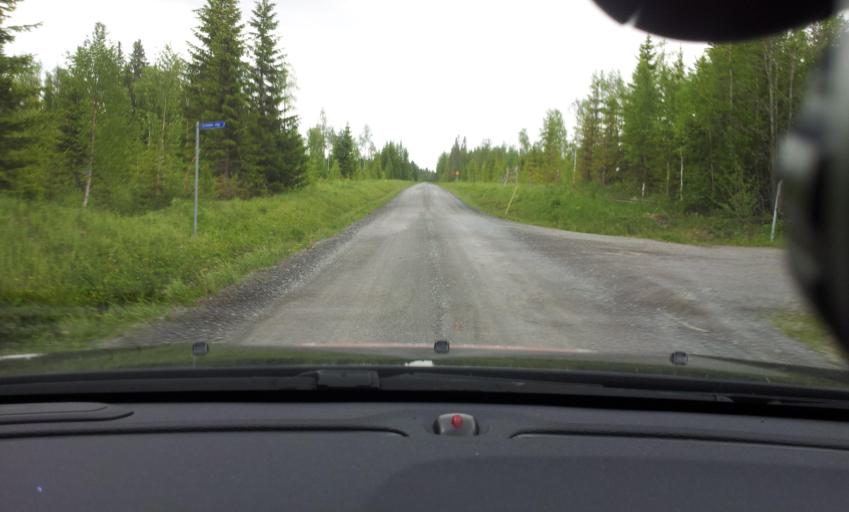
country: SE
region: Jaemtland
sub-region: OEstersunds Kommun
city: Brunflo
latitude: 63.1441
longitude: 15.0486
